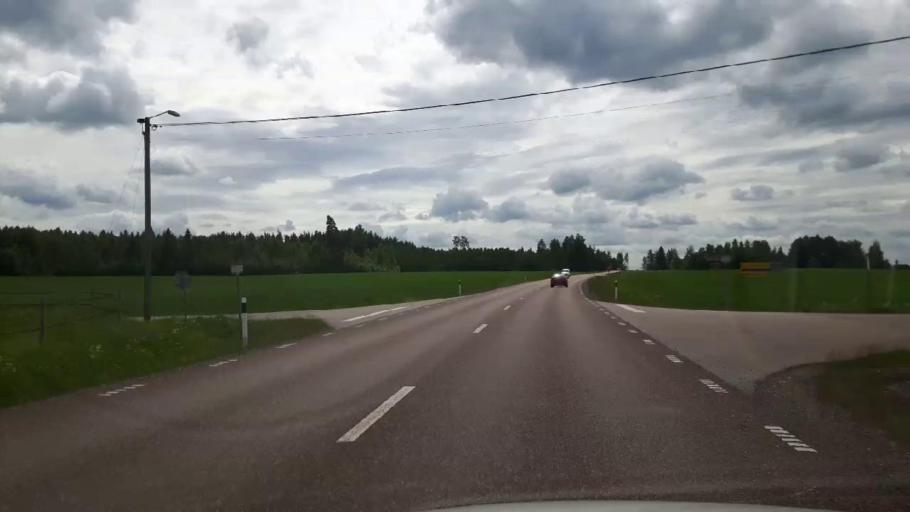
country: SE
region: Dalarna
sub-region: Hedemora Kommun
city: Hedemora
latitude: 60.3419
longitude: 15.9458
